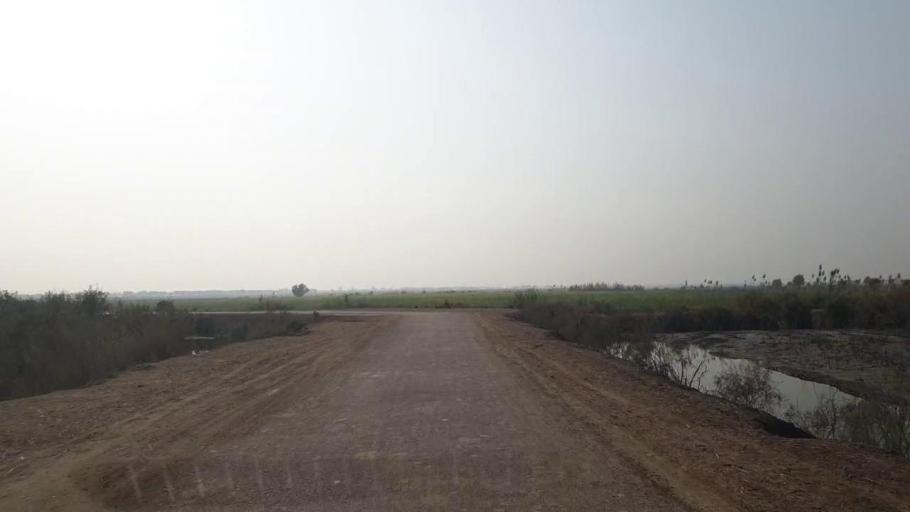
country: PK
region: Sindh
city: Shahdadpur
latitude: 25.9696
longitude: 68.5159
